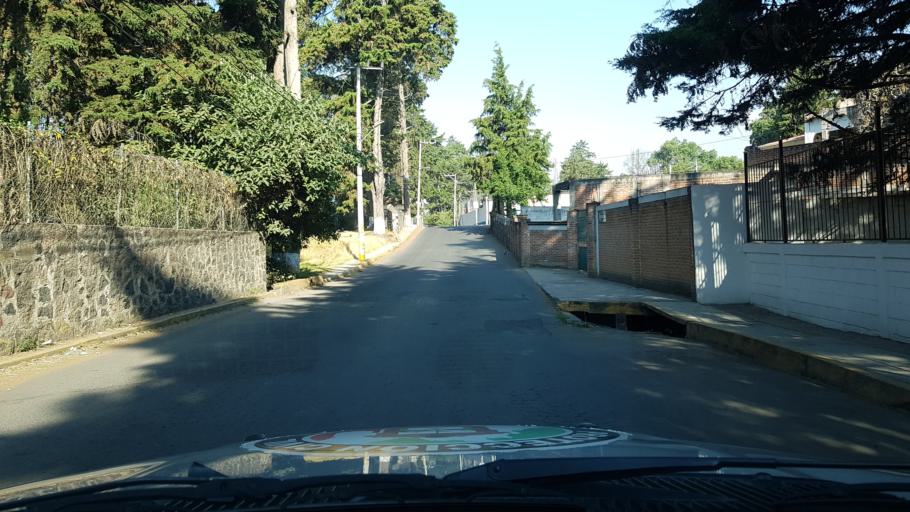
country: MX
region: Mexico
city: Ozumba de Alzate
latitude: 19.0615
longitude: -98.7806
